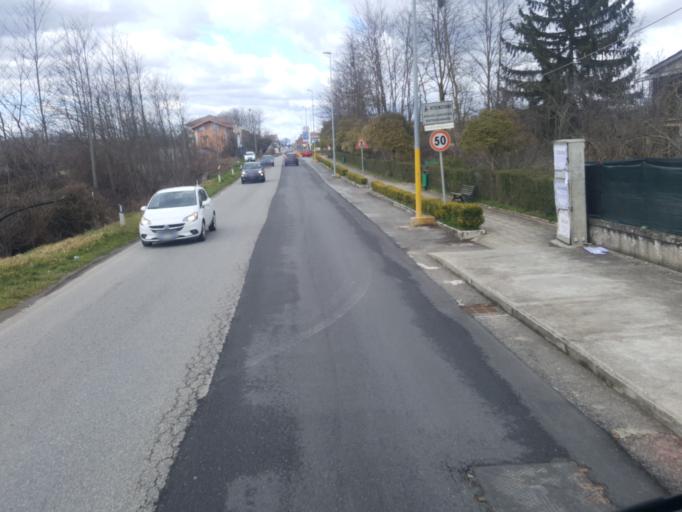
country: IT
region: Calabria
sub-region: Provincia di Cosenza
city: Santo Stefano di Rogliano
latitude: 39.2045
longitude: 16.3118
